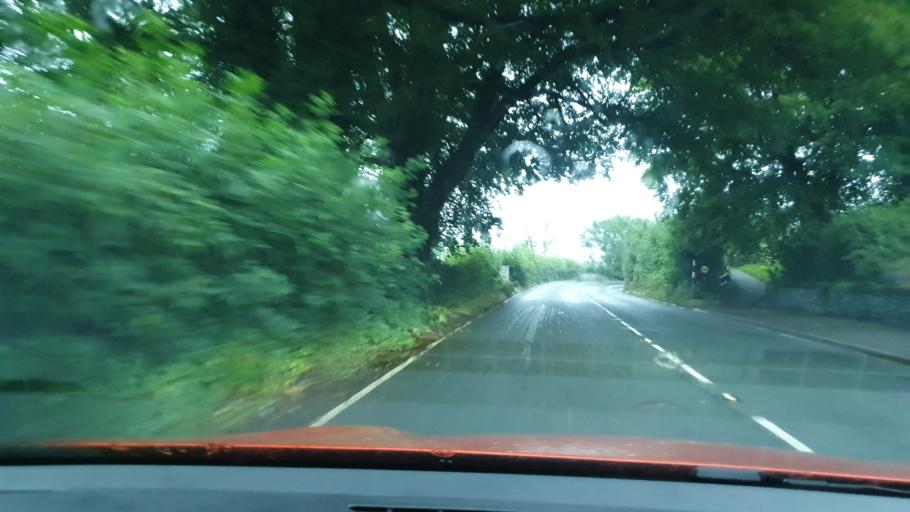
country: GB
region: England
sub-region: Cumbria
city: Ulverston
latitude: 54.2370
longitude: -3.0571
